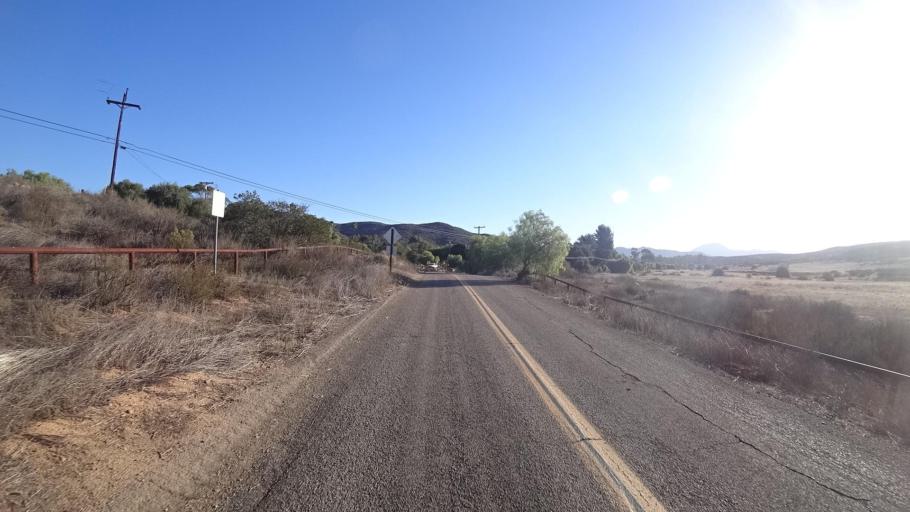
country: US
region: California
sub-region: San Diego County
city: Jamul
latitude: 32.7025
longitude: -116.9028
